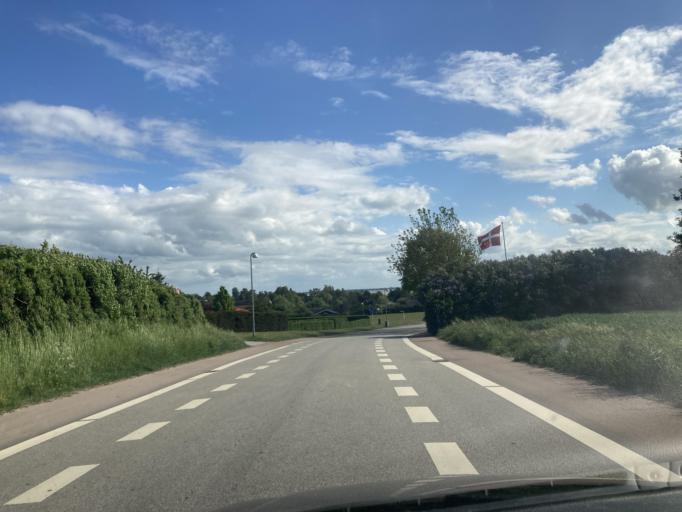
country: DK
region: Capital Region
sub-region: Gribskov Kommune
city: Helsinge
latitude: 56.0110
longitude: 12.1118
